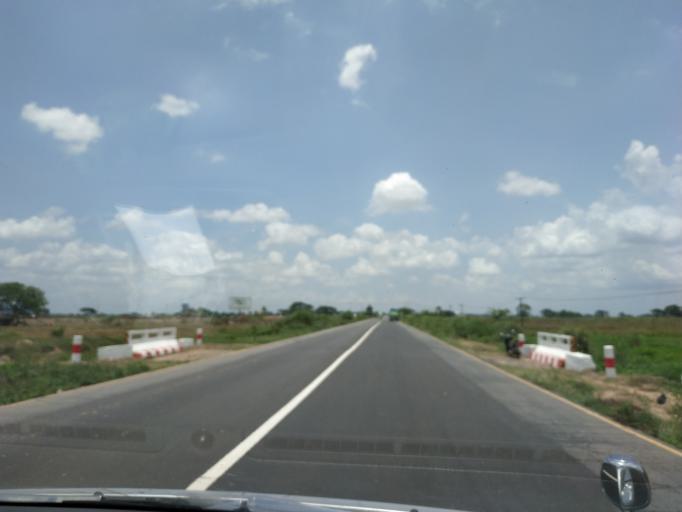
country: MM
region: Bago
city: Thanatpin
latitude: 17.4573
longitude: 96.6048
